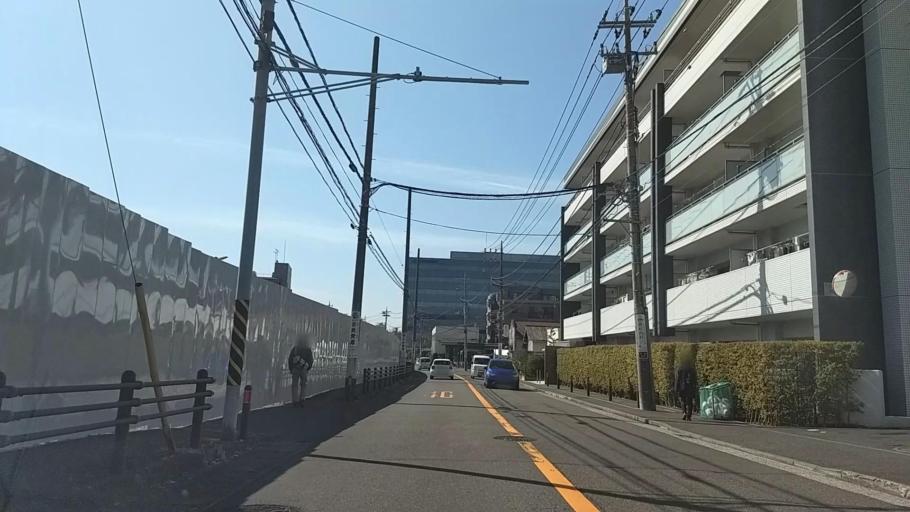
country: JP
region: Kanagawa
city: Kamakura
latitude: 35.3570
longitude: 139.5376
